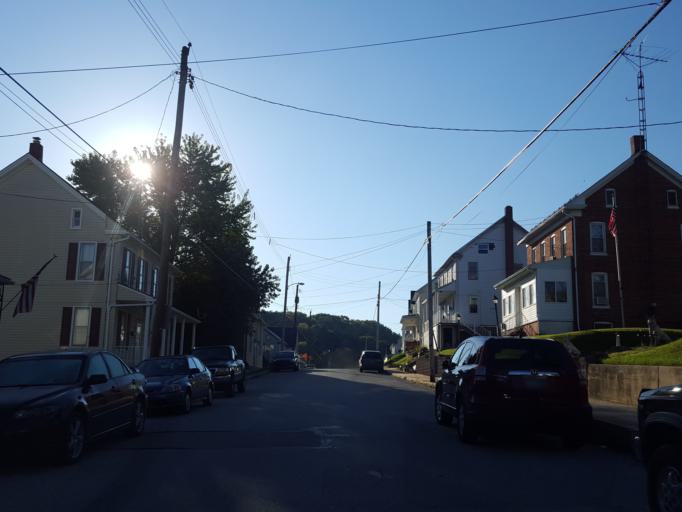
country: US
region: Pennsylvania
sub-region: York County
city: Yoe
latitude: 39.9104
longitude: -76.6391
